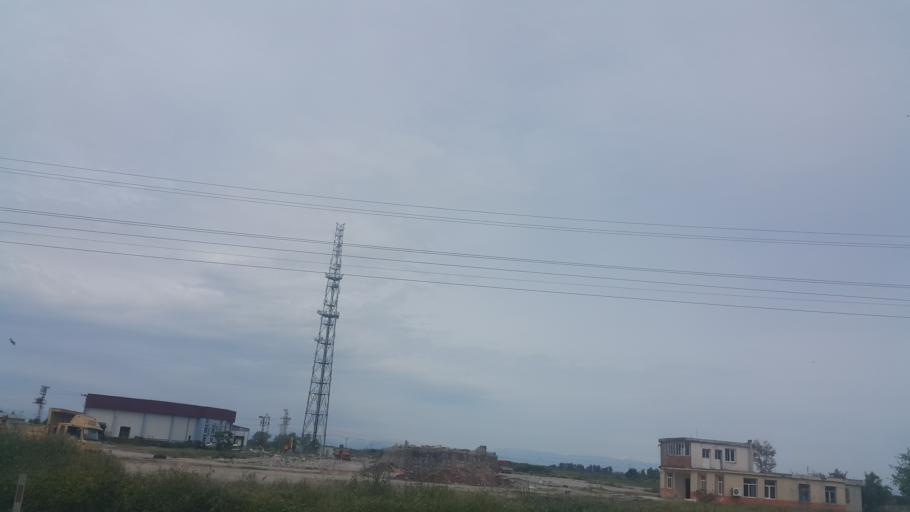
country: TR
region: Adana
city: Ceyhan
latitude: 37.0521
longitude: 35.8109
